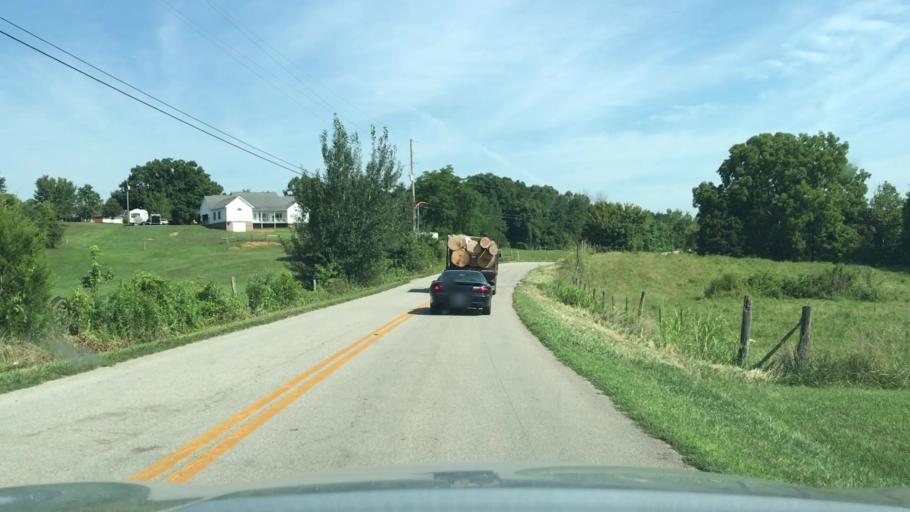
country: US
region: Kentucky
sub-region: Clinton County
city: Albany
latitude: 36.7573
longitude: -84.9977
